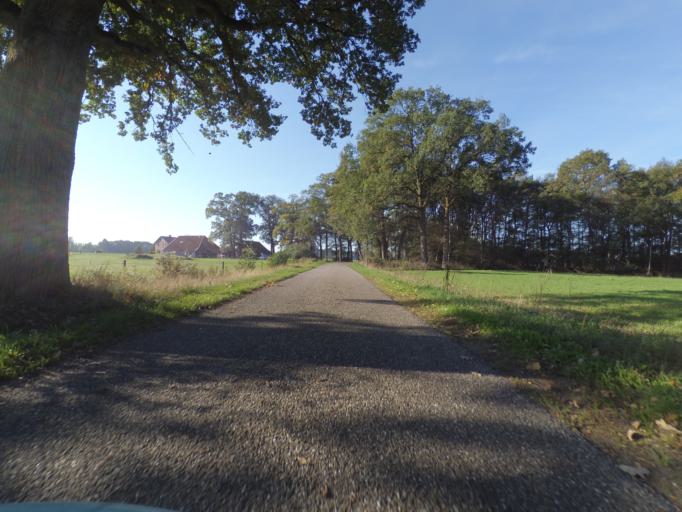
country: NL
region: Gelderland
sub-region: Berkelland
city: Eibergen
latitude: 52.0861
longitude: 6.6916
